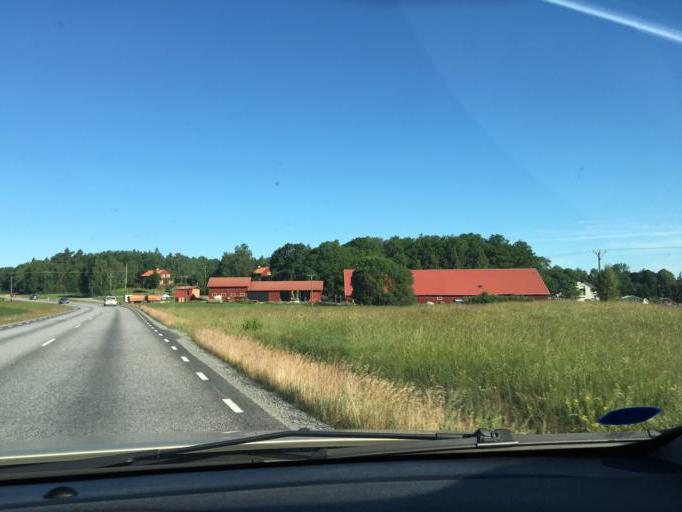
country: SE
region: Stockholm
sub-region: Salems Kommun
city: Ronninge
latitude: 59.2199
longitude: 17.7546
